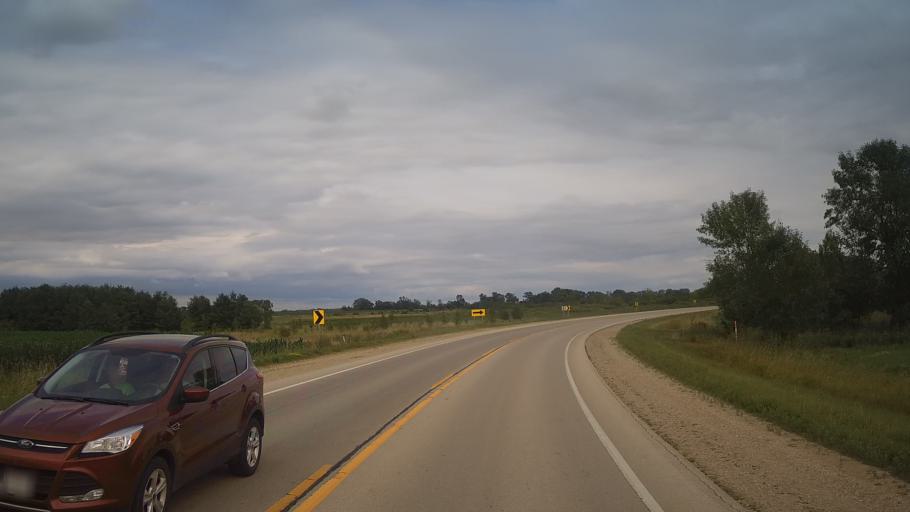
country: US
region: Wisconsin
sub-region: Green Lake County
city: Berlin
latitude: 44.0482
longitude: -88.9728
